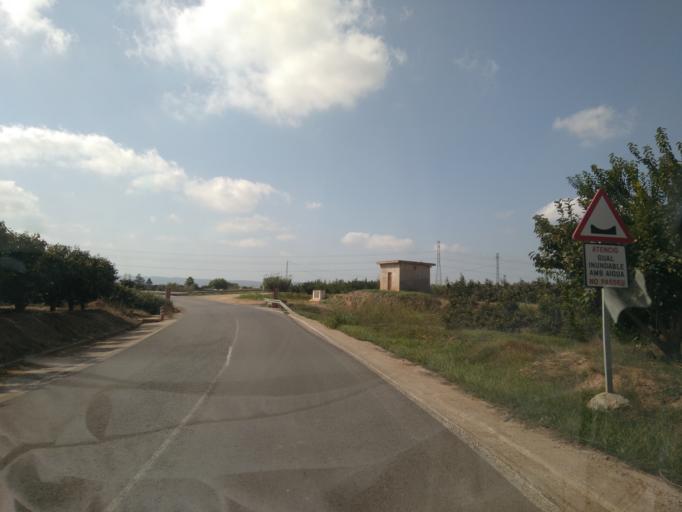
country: ES
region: Valencia
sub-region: Provincia de Valencia
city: L'Alcudia
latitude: 39.1914
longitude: -0.5201
